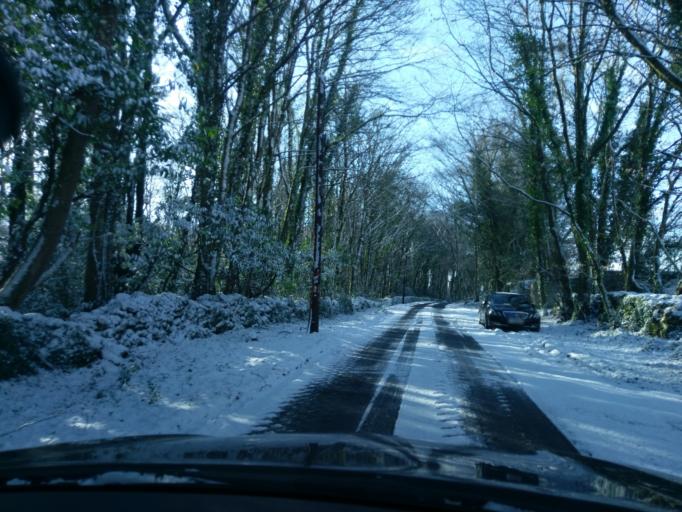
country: IE
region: Connaught
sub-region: County Galway
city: Gort
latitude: 53.1796
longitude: -8.8017
